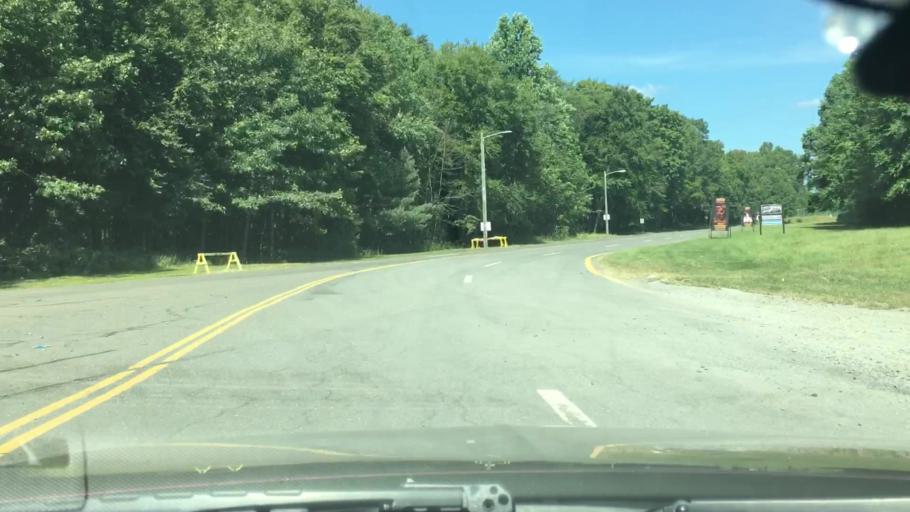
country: US
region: Connecticut
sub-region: Hartford County
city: Bristol
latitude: 41.6432
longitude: -72.9193
